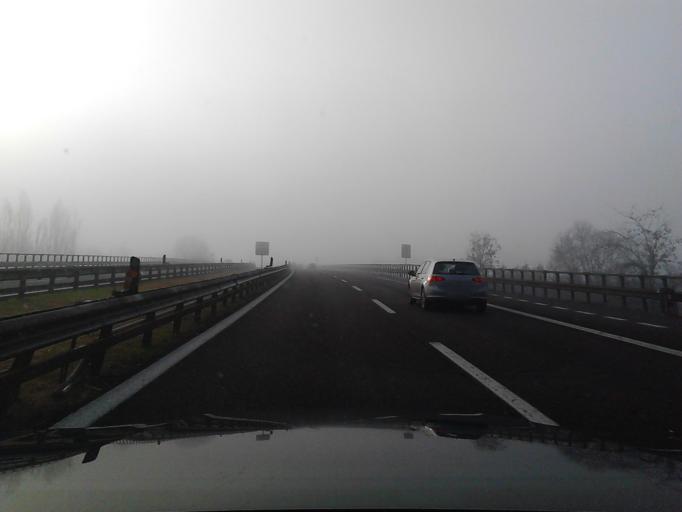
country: IT
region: Veneto
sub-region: Provincia di Verona
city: Dossobuono
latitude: 45.3903
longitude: 10.9082
